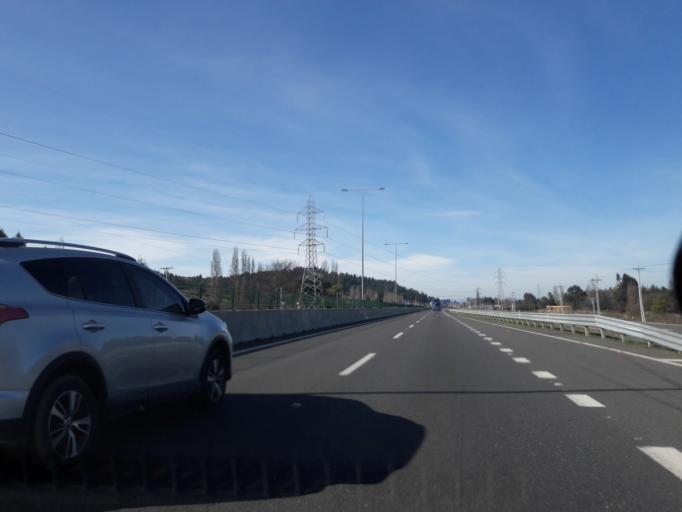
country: CL
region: Biobio
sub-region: Provincia de Biobio
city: Yumbel
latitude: -36.9963
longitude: -72.5874
